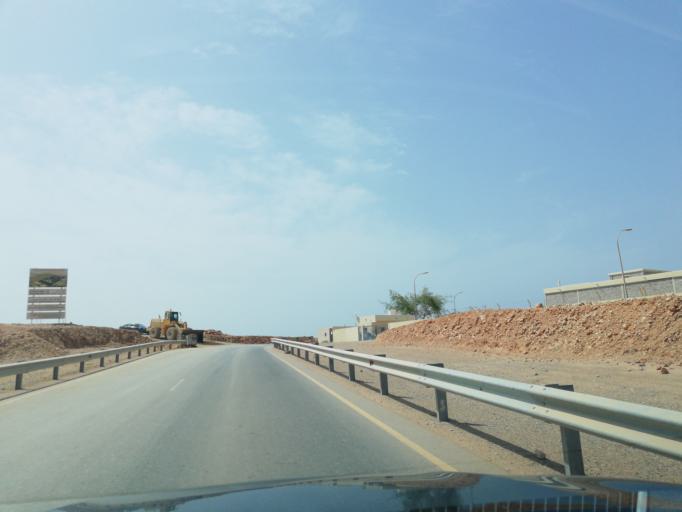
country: OM
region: Muhafazat Masqat
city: Bawshar
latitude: 23.5549
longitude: 58.3375
